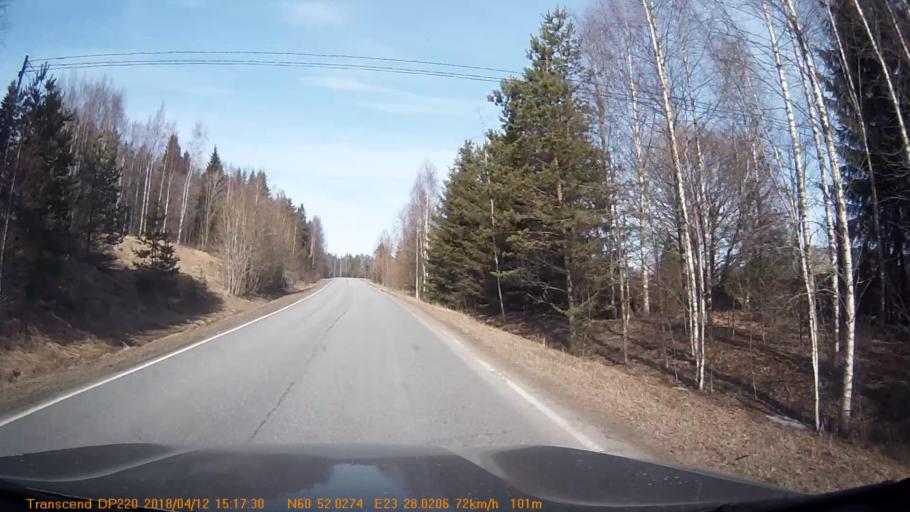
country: FI
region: Haeme
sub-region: Forssa
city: Jokioinen
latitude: 60.8675
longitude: 23.4678
